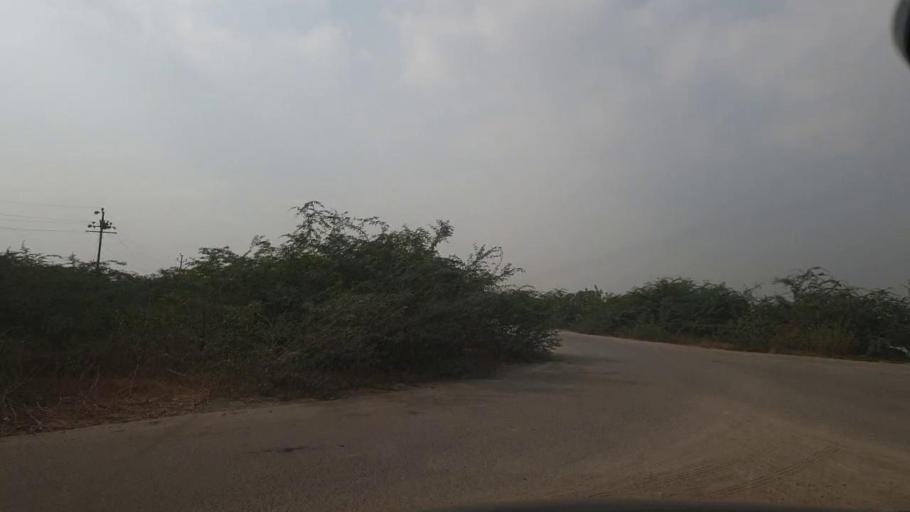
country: PK
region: Sindh
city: Malir Cantonment
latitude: 24.9469
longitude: 67.2943
